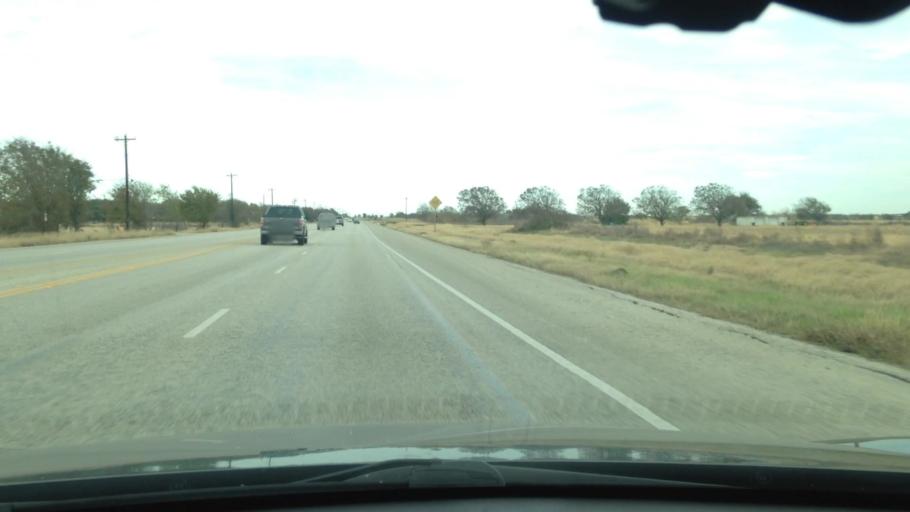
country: US
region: Texas
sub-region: Caldwell County
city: Martindale
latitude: 29.9040
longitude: -97.8665
